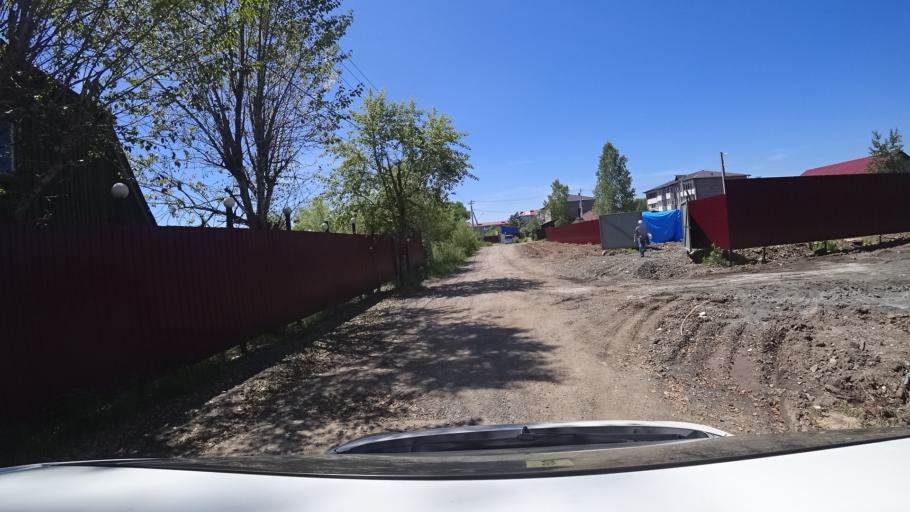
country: RU
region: Khabarovsk Krai
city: Topolevo
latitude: 48.5097
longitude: 135.1788
